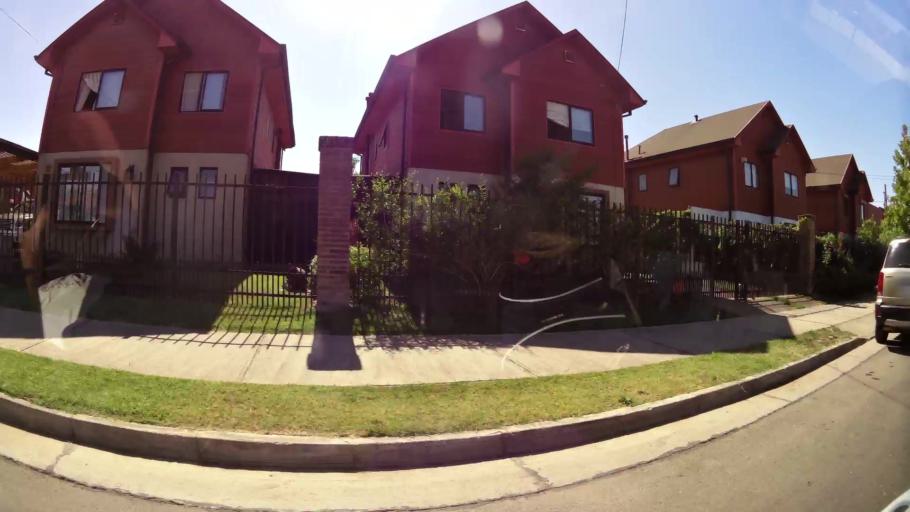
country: CL
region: Maule
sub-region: Provincia de Talca
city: Talca
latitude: -35.4283
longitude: -71.6150
